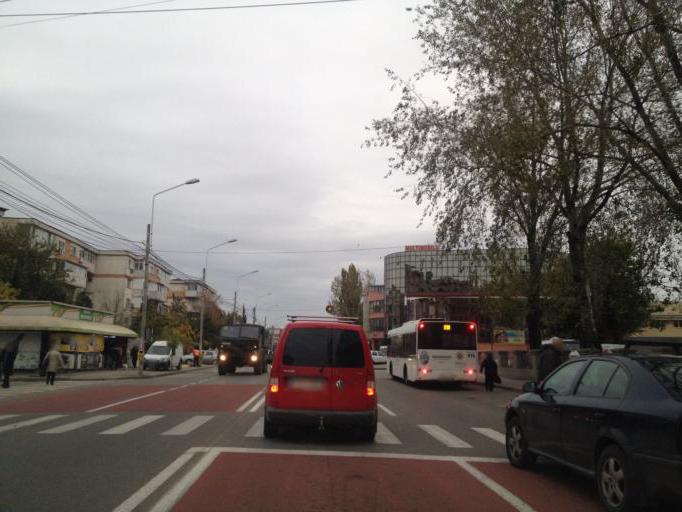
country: RO
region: Dolj
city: Craiova
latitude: 44.3157
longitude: 23.8342
